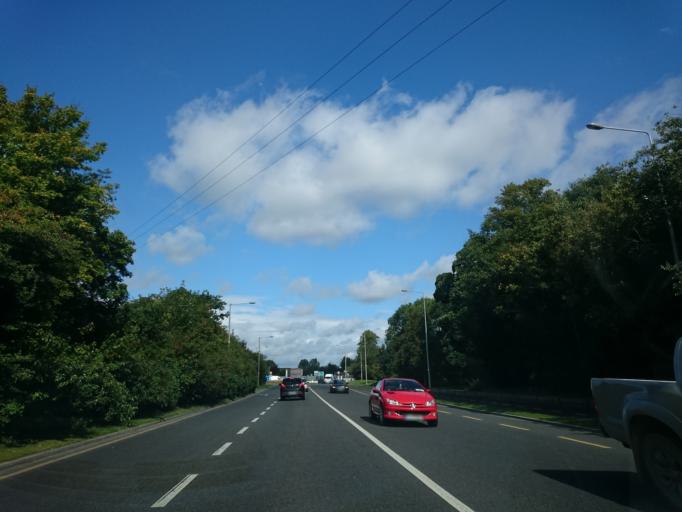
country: IE
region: Leinster
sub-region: Kilkenny
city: Kilkenny
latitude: 52.6416
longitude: -7.2617
